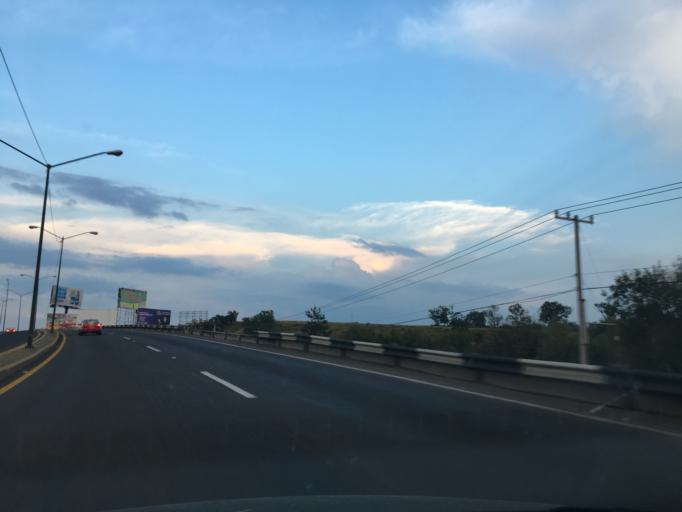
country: MX
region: Michoacan
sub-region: Morelia
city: Morelos
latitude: 19.6646
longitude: -101.2269
